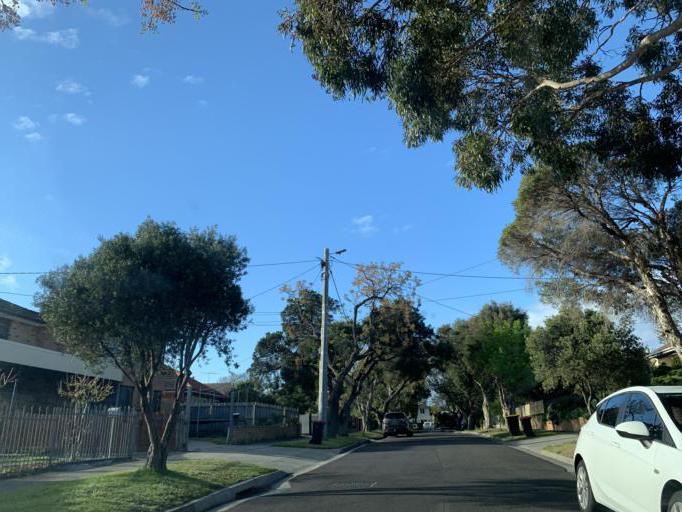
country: AU
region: Victoria
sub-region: Kingston
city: Mentone
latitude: -37.9818
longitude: 145.0596
